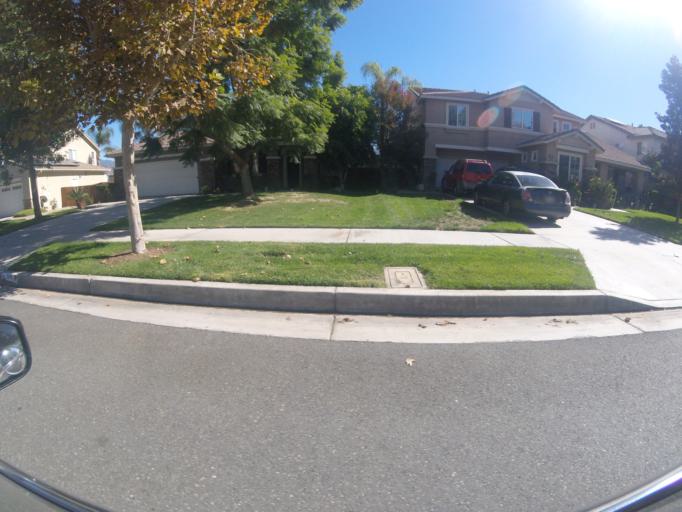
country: US
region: California
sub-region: San Bernardino County
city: Mentone
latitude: 34.0761
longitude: -117.1472
